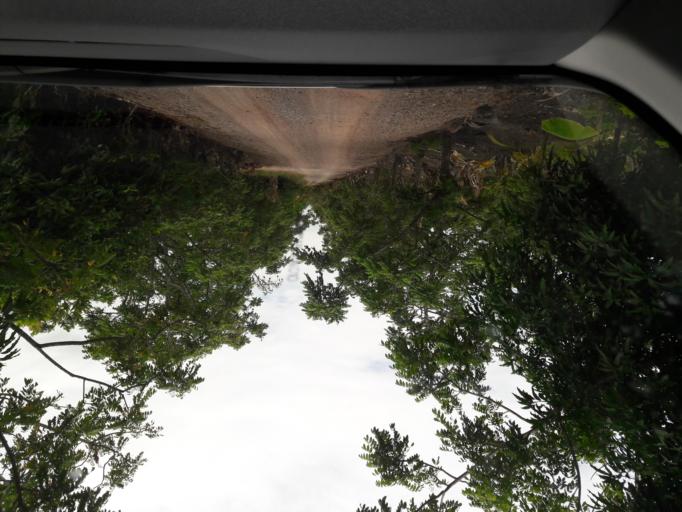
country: TH
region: Ratchaburi
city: Damnoen Saduak
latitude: 13.5554
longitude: 100.0019
